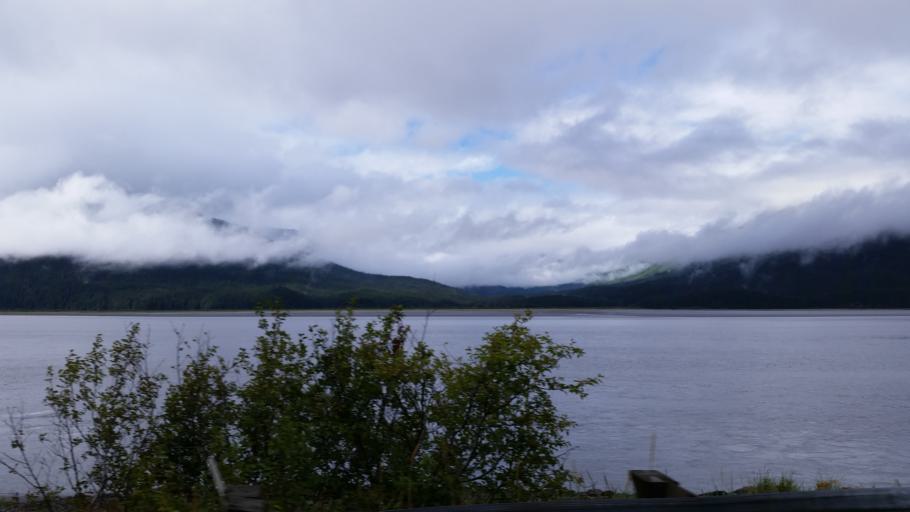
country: US
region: Alaska
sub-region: Anchorage Municipality
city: Girdwood
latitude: 60.8575
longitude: -149.0138
